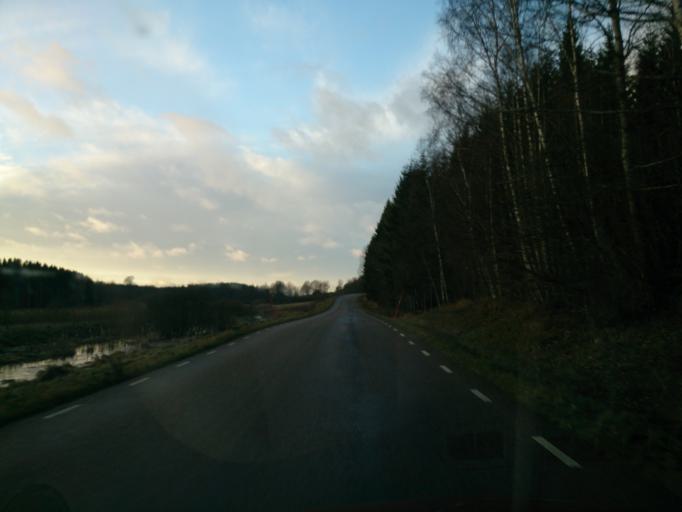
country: SE
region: OEstergoetland
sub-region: Atvidabergs Kommun
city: Atvidaberg
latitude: 58.2894
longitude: 16.0123
